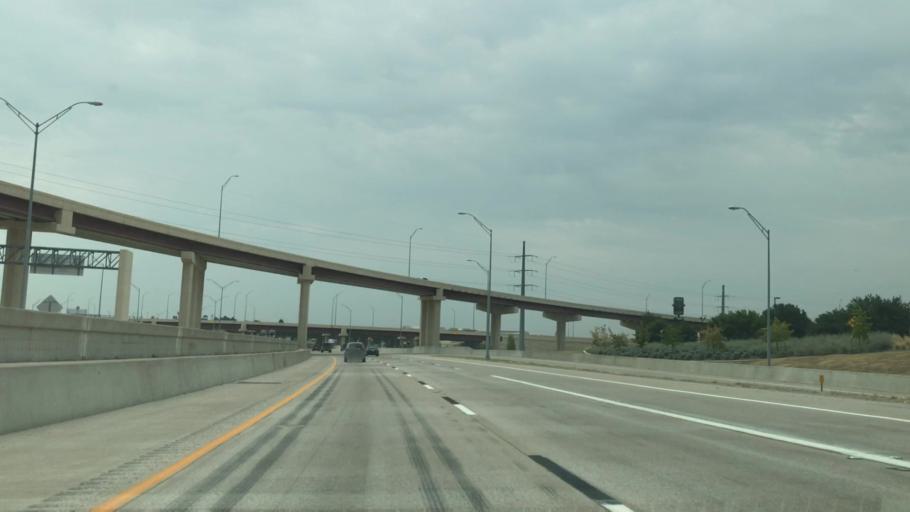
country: US
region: Texas
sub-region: Tarrant County
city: Grapevine
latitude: 32.9247
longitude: -97.0881
